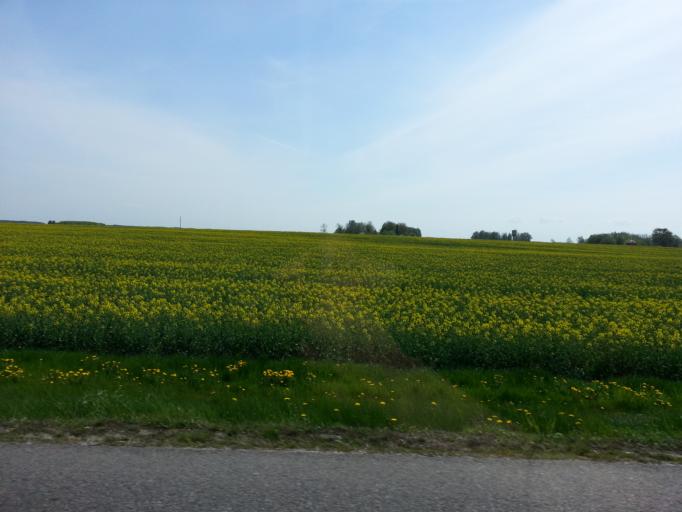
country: LT
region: Panevezys
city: Pasvalys
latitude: 56.0035
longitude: 24.3496
